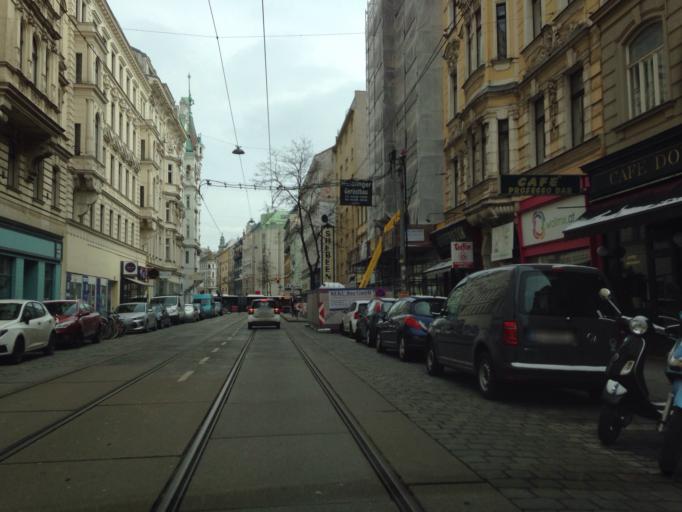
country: AT
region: Vienna
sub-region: Wien Stadt
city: Vienna
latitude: 48.2066
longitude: 16.3479
